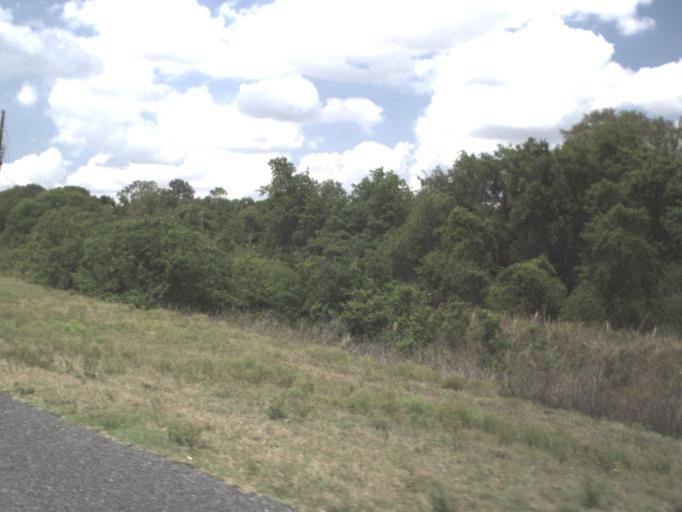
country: US
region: Florida
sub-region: Sumter County
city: Wildwood
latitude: 28.8245
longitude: -81.9770
